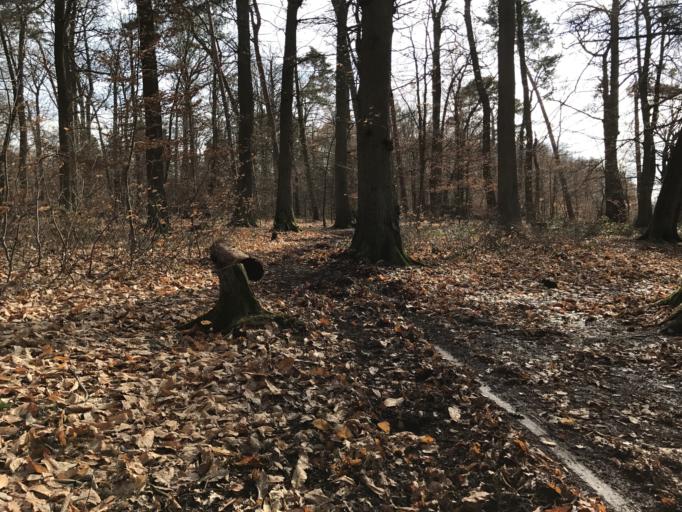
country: DE
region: Hesse
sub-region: Regierungsbezirk Darmstadt
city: Walluf
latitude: 50.0670
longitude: 8.1781
